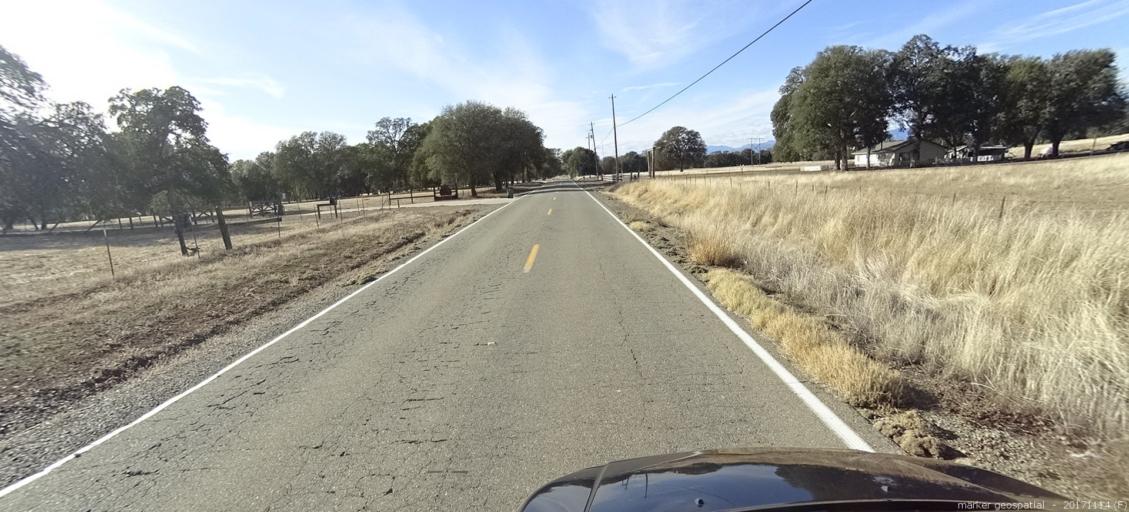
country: US
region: California
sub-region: Shasta County
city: Anderson
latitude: 40.3881
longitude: -122.4718
